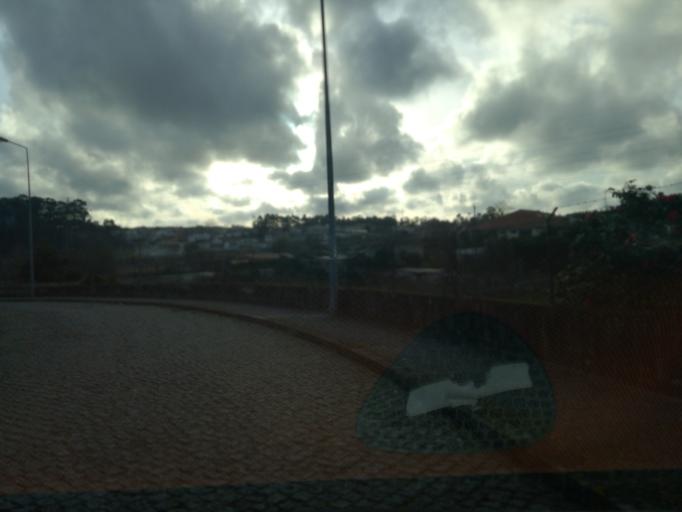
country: PT
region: Porto
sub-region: Maia
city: Nogueira
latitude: 41.2537
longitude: -8.6021
